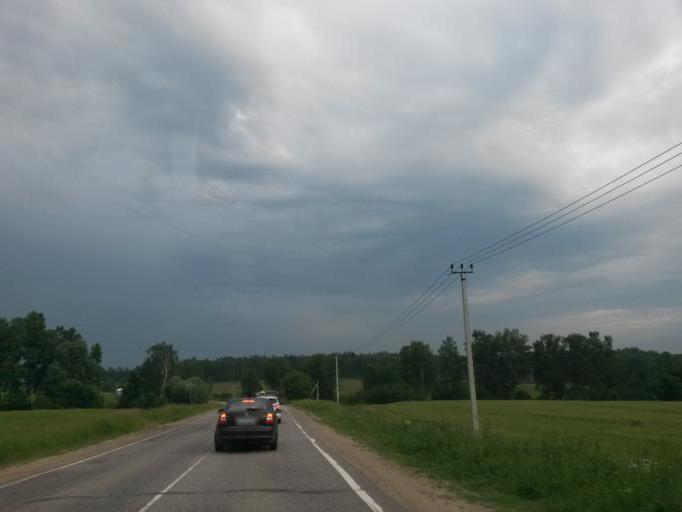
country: RU
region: Moskovskaya
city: Vostryakovo
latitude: 55.3479
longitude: 37.7274
